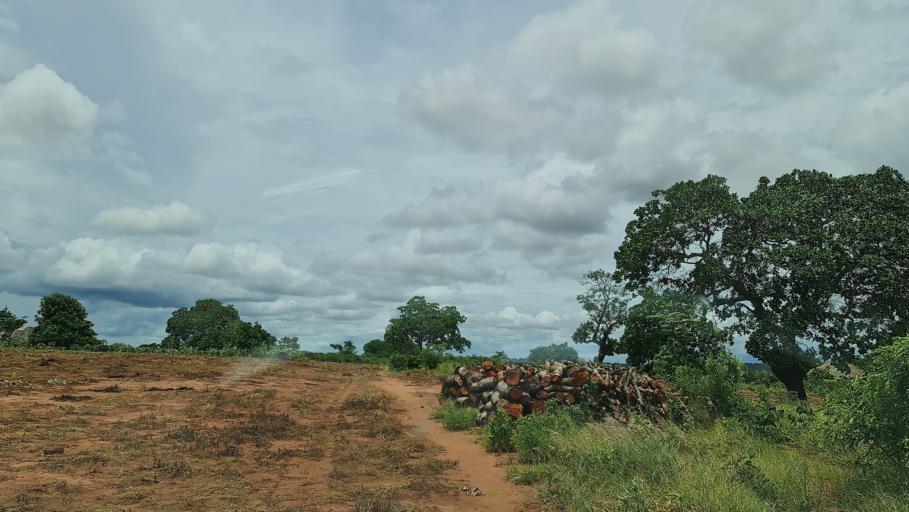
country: MZ
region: Nampula
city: Nacala
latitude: -14.7862
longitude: 39.9796
